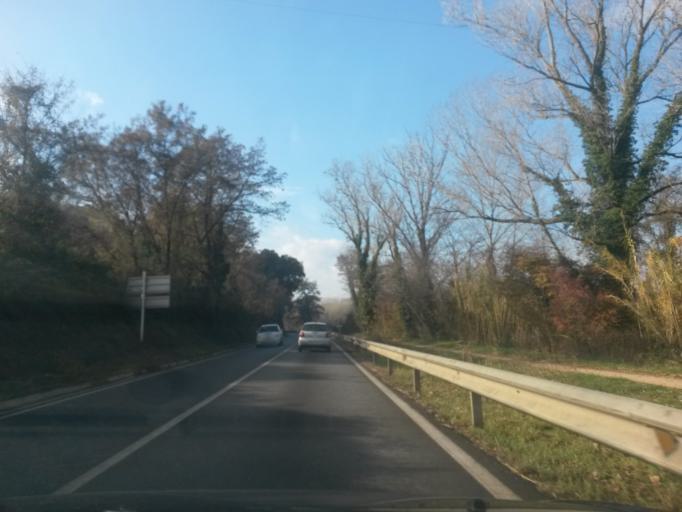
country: ES
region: Catalonia
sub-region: Provincia de Girona
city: Vilablareix
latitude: 41.9707
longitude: 2.7595
